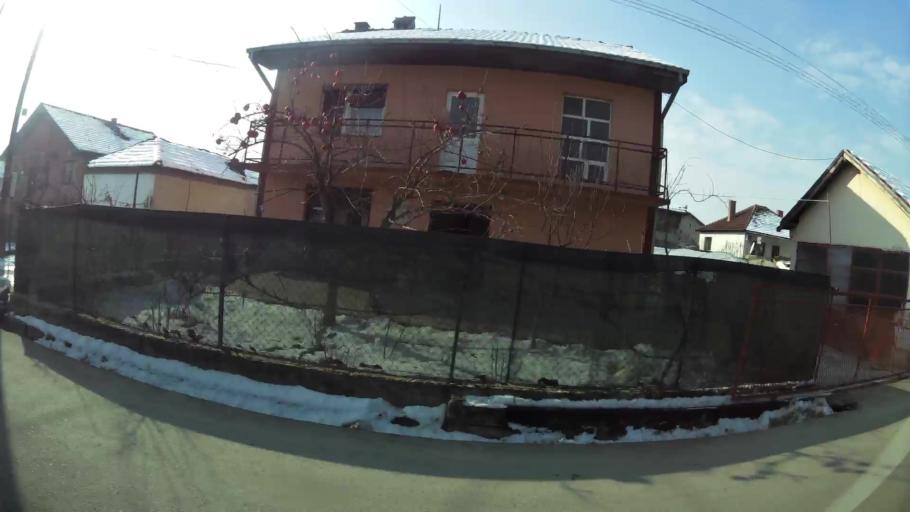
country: MK
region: Suto Orizari
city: Suto Orizare
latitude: 42.0275
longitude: 21.3763
